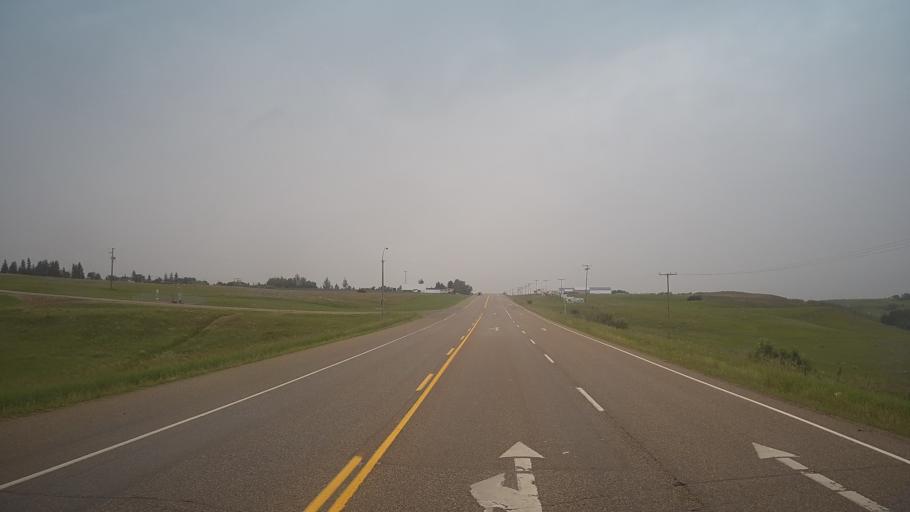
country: CA
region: Saskatchewan
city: Biggar
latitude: 52.0592
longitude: -107.9636
